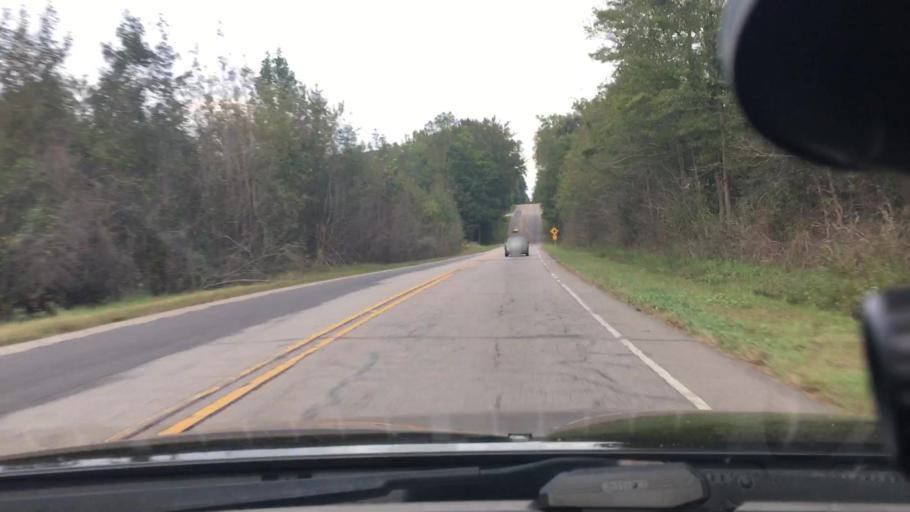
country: US
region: North Carolina
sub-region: Moore County
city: Carthage
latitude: 35.3674
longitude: -79.3128
